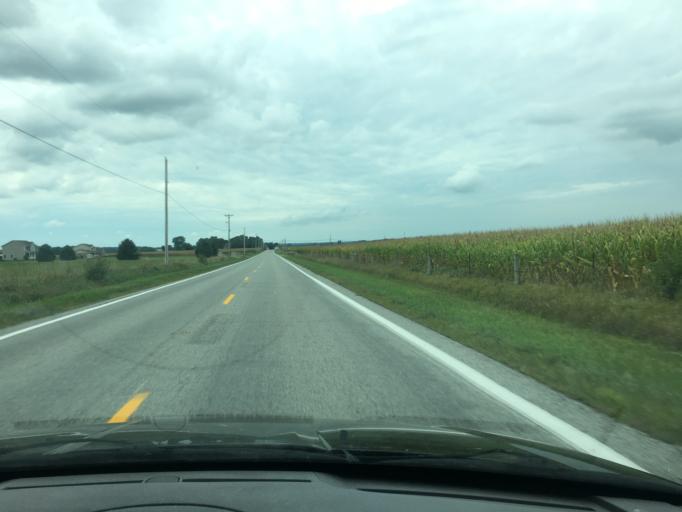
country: US
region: Ohio
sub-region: Champaign County
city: Urbana
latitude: 40.1538
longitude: -83.7222
